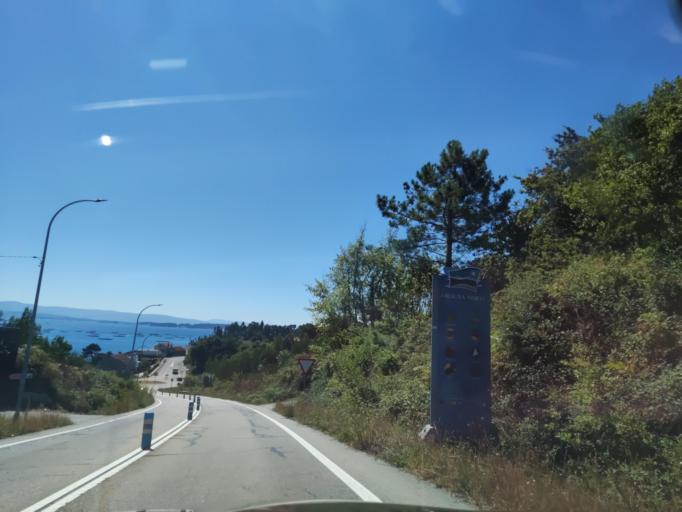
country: ES
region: Galicia
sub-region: Provincia da Coruna
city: Boiro
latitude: 42.6223
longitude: -8.9256
